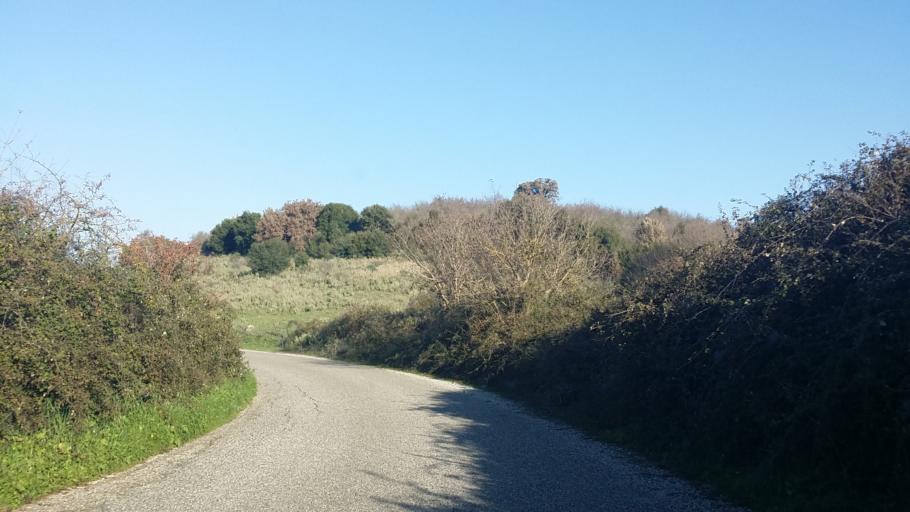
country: GR
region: West Greece
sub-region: Nomos Aitolias kai Akarnanias
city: Katouna
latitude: 38.7602
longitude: 21.1428
